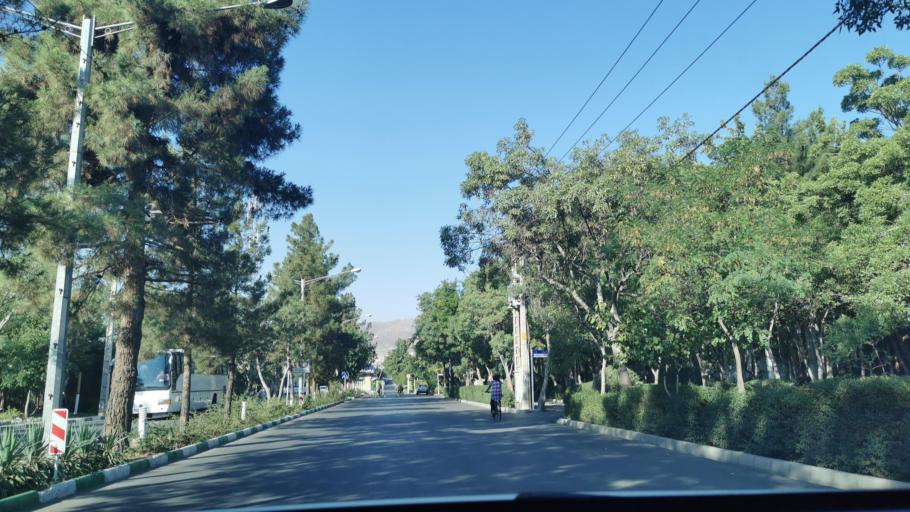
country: IR
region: Razavi Khorasan
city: Mashhad
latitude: 36.3132
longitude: 59.5233
